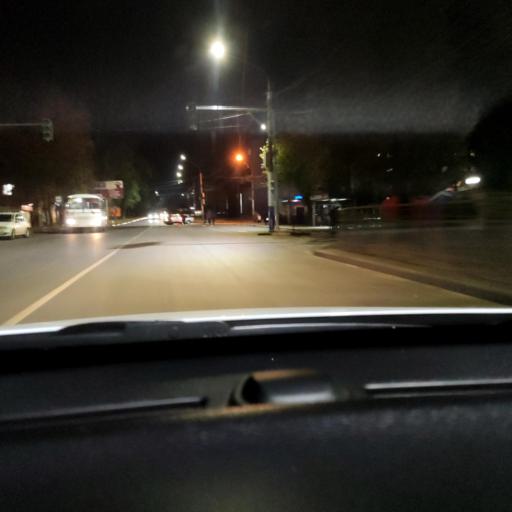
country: RU
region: Voronezj
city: Somovo
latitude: 51.7204
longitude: 39.2712
